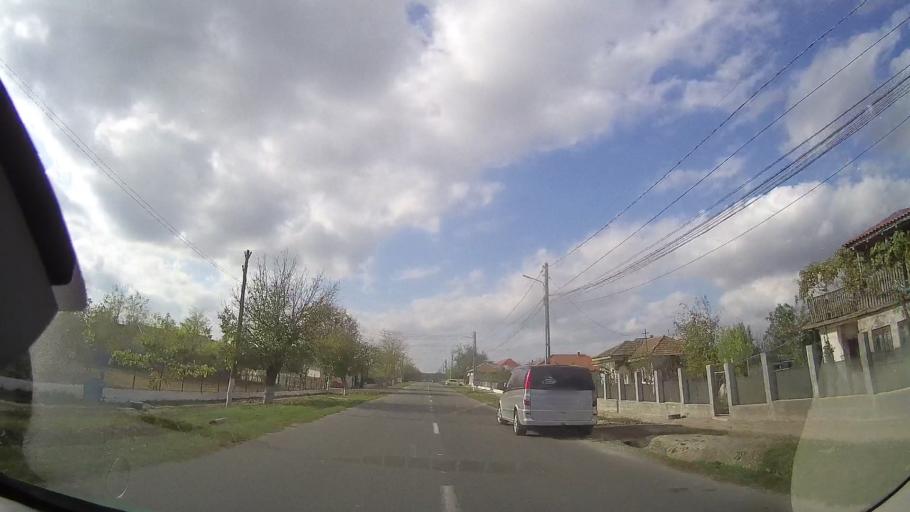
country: RO
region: Constanta
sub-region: Comuna Pecineaga
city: Pecineaga
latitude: 43.8951
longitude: 28.5055
